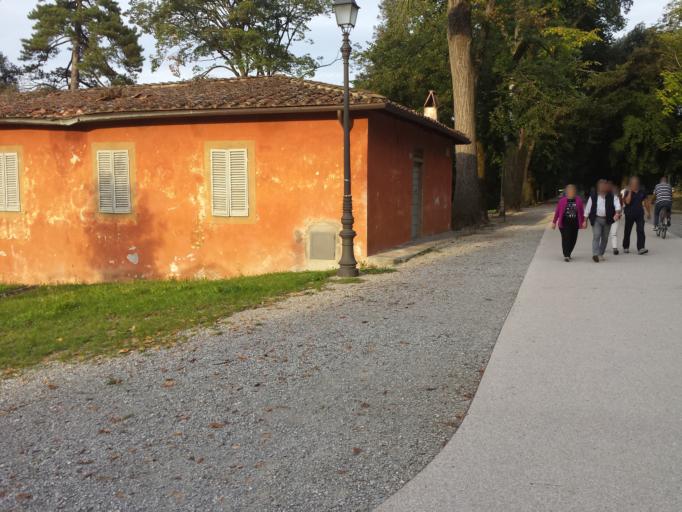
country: IT
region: Tuscany
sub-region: Provincia di Lucca
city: Lucca
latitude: 43.8407
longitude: 10.5103
